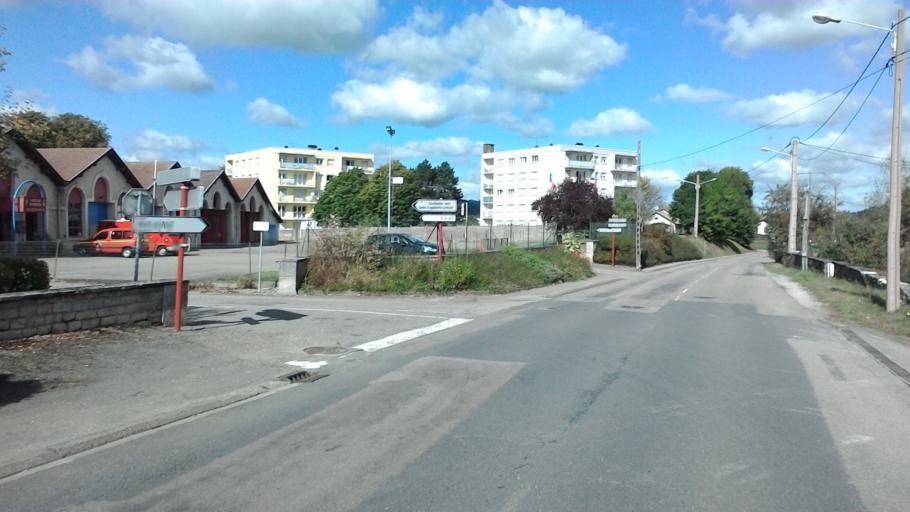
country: FR
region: Lorraine
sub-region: Departement des Vosges
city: Neufchateau
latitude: 48.3567
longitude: 5.6825
